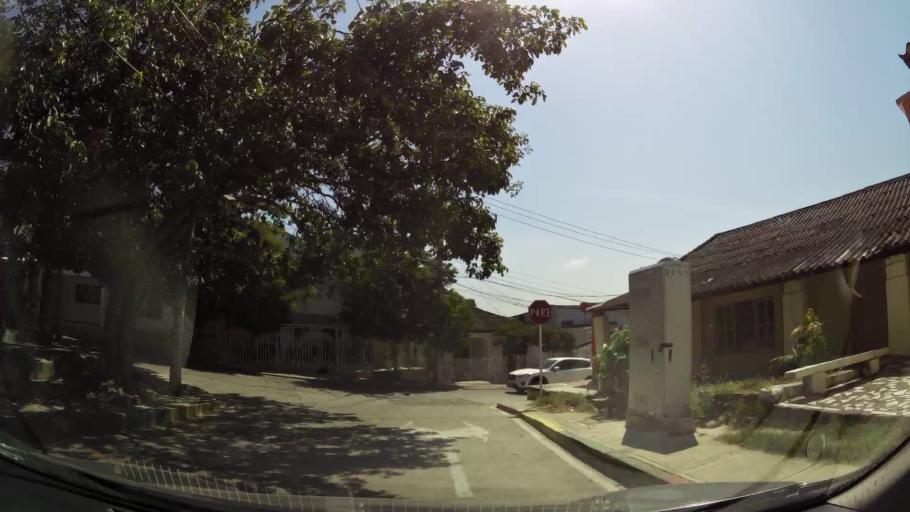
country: CO
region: Bolivar
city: Cartagena
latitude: 10.3898
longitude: -75.5131
